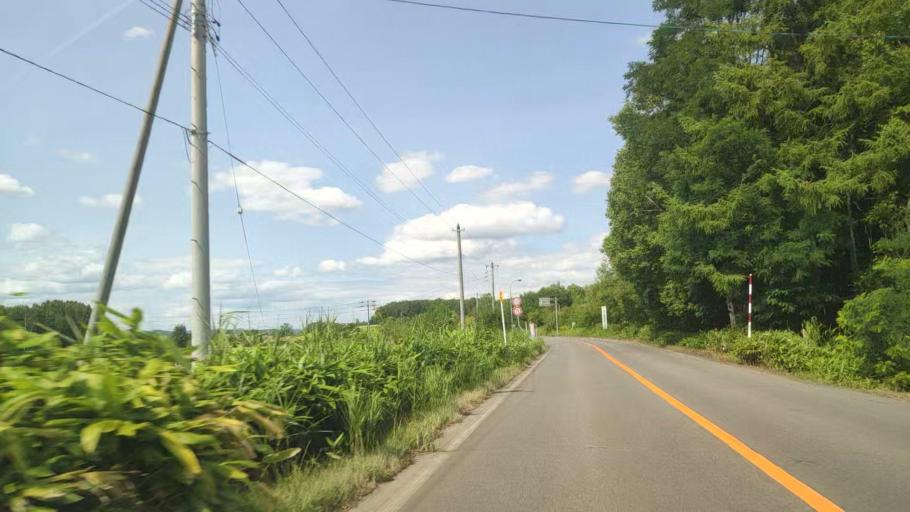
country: JP
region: Hokkaido
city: Nayoro
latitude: 44.2755
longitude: 142.4229
